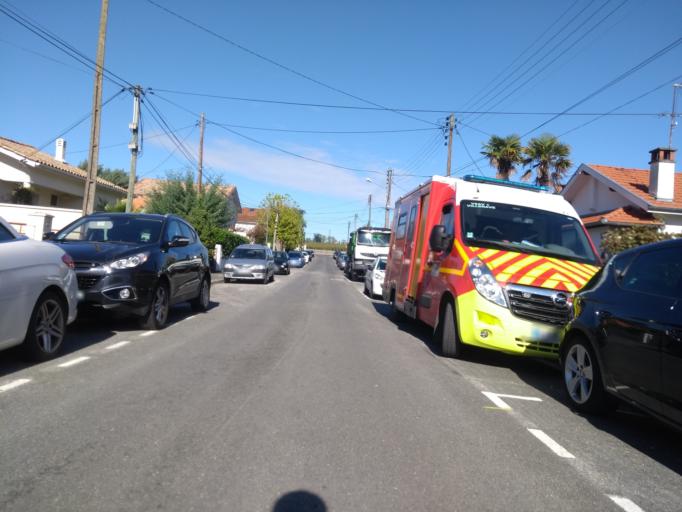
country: FR
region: Aquitaine
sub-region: Departement de la Gironde
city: Talence
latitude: 44.8071
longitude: -0.6132
